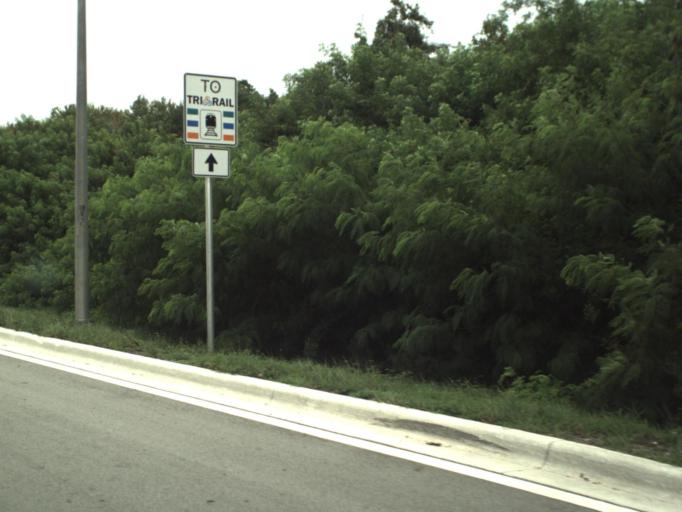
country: US
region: Florida
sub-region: Palm Beach County
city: Boca Del Mar
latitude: 26.3509
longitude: -80.1218
